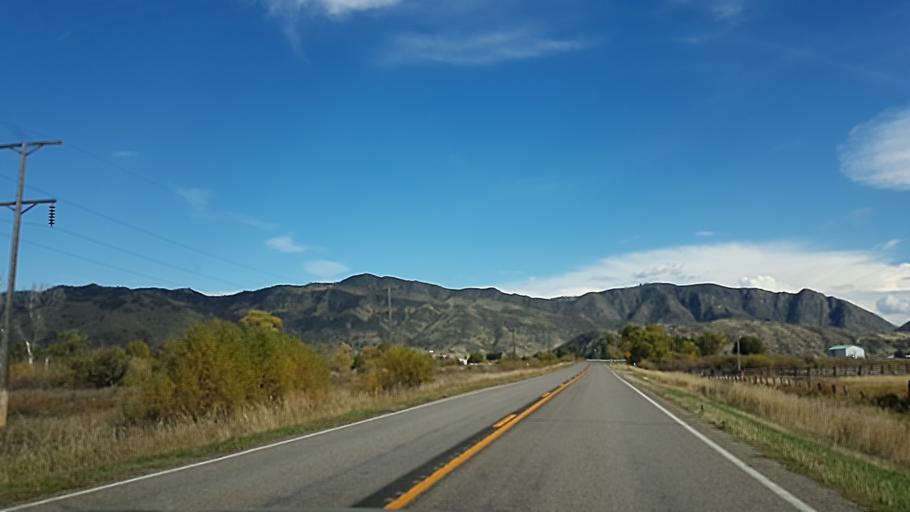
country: US
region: Montana
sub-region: Jefferson County
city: Whitehall
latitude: 45.8522
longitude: -111.9453
